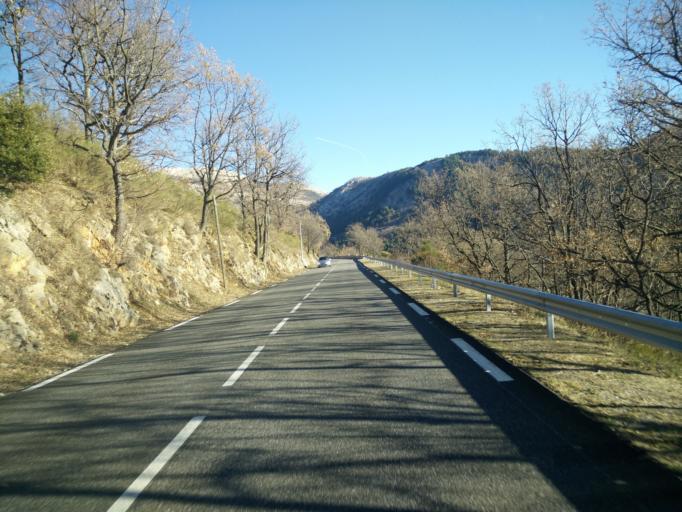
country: FR
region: Provence-Alpes-Cote d'Azur
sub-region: Departement des Alpes-Maritimes
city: Saint-Vallier-de-Thiey
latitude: 43.7169
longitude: 6.8385
